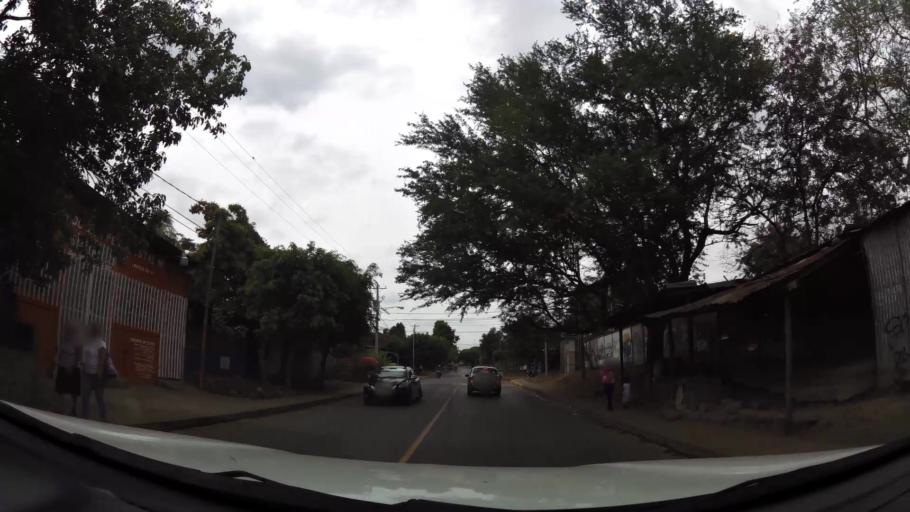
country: NI
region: Managua
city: Managua
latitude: 12.1187
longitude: -86.1959
